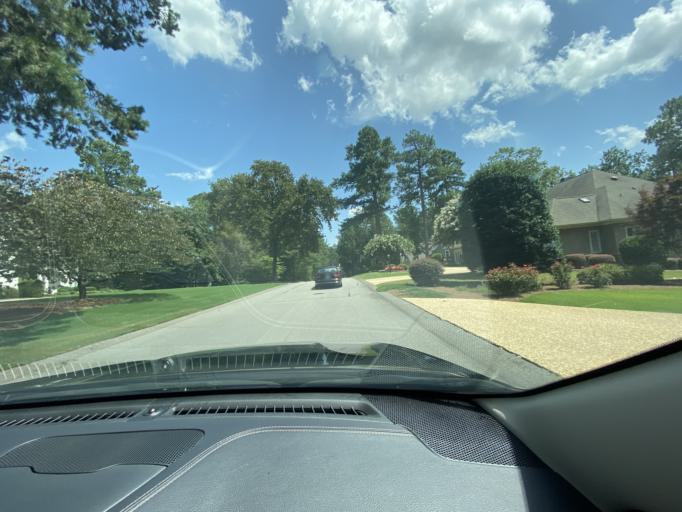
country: US
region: North Carolina
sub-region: Moore County
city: Pinehurst
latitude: 35.1989
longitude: -79.4400
